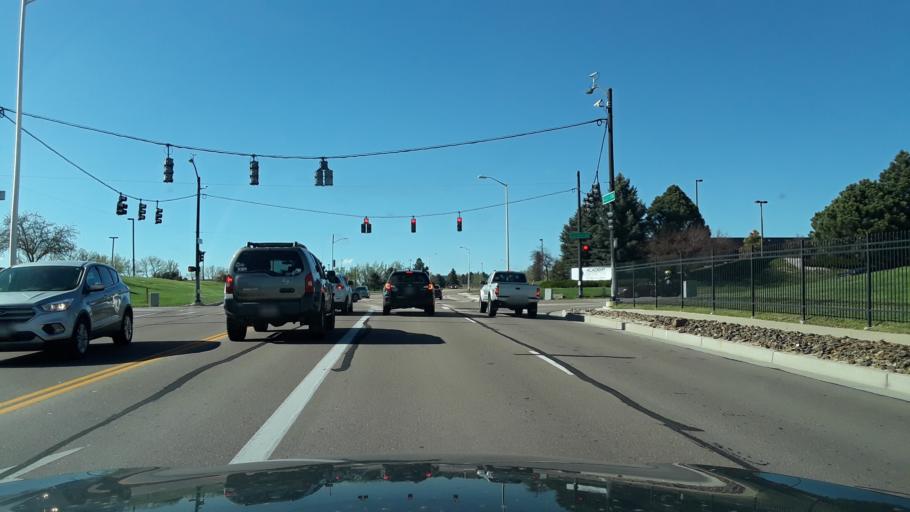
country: US
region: Colorado
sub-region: El Paso County
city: Air Force Academy
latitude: 38.9521
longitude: -104.7916
